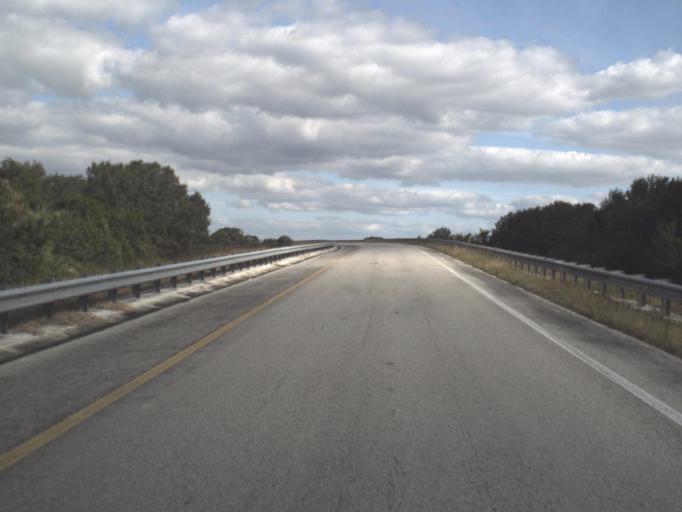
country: US
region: Florida
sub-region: Brevard County
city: Port Saint John
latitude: 28.4522
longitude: -80.8776
